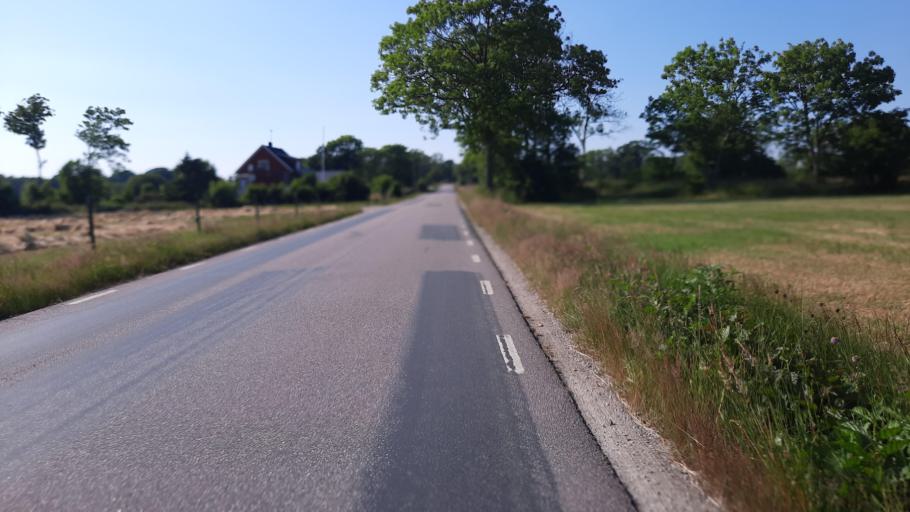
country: SE
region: Blekinge
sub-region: Karlskrona Kommun
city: Sturko
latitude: 56.1080
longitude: 15.6852
